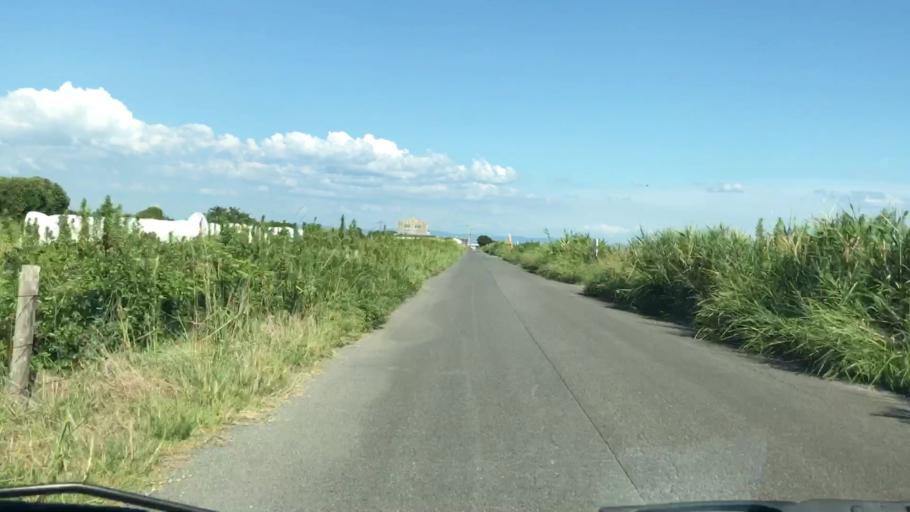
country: JP
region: Saga Prefecture
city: Okawa
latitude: 33.1517
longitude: 130.3149
